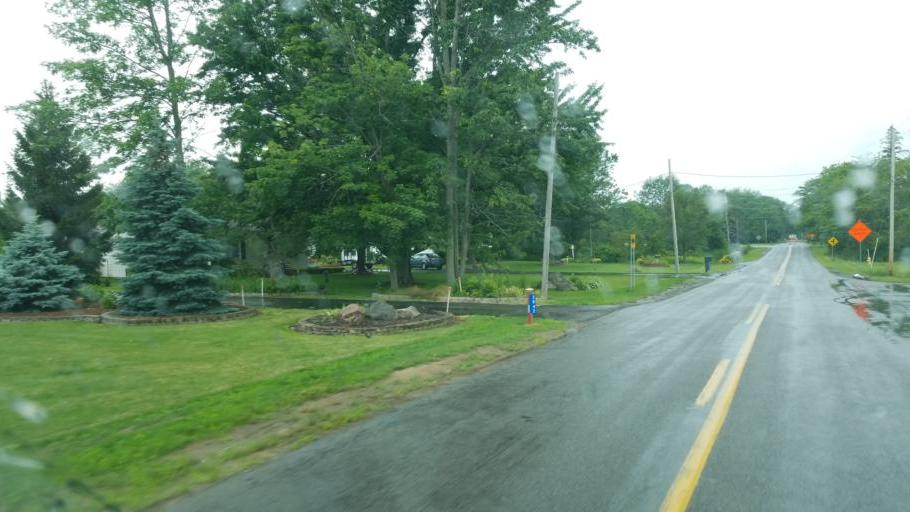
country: US
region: New York
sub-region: Niagara County
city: Ransomville
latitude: 43.2640
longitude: -78.8900
